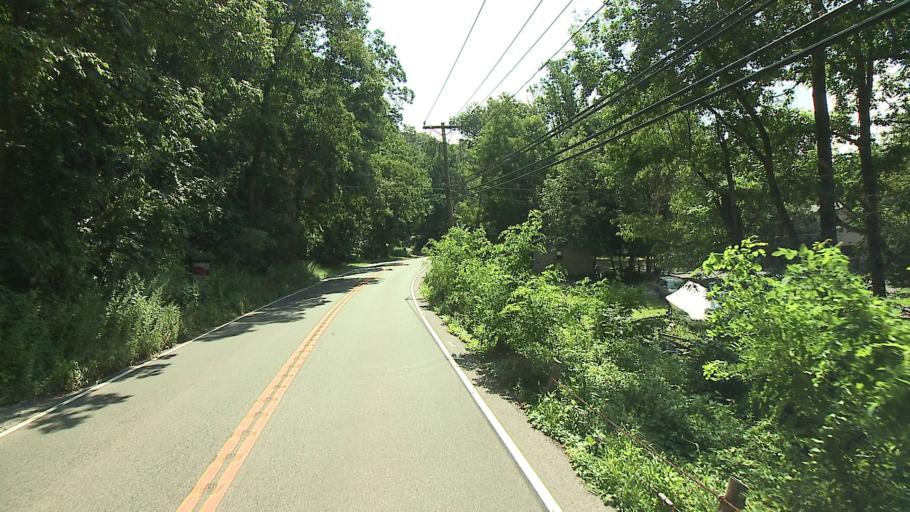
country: US
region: Connecticut
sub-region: Fairfield County
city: Sherman
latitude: 41.5160
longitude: -73.4744
